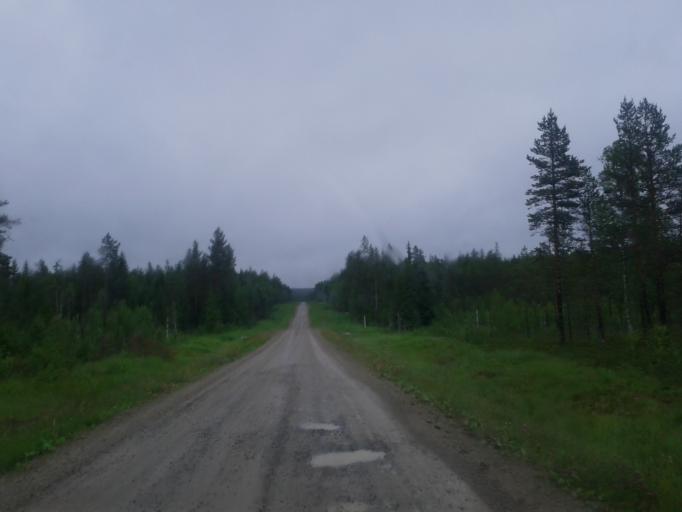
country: SE
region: Vaesternorrland
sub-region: Ange Kommun
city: Fransta
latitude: 62.2356
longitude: 16.3098
